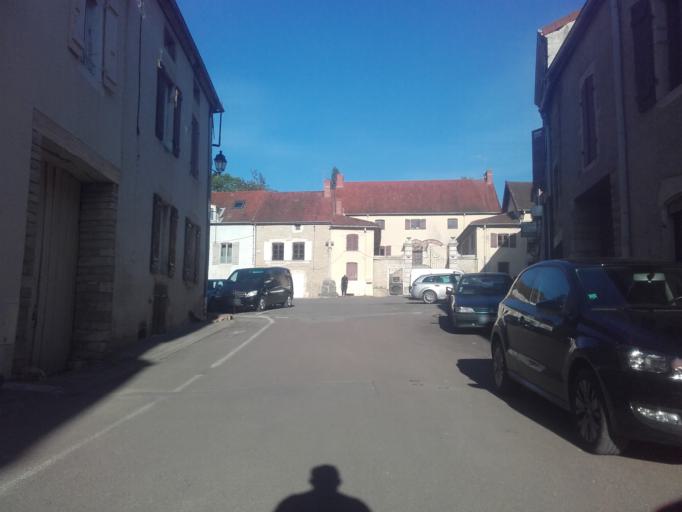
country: FR
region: Bourgogne
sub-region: Departement de Saone-et-Loire
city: Rully
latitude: 46.8747
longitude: 4.7432
